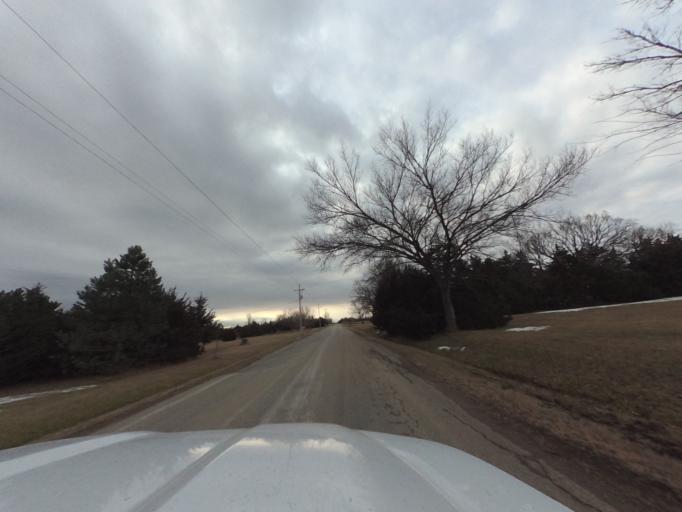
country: US
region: Kansas
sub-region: Chase County
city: Cottonwood Falls
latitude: 38.4289
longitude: -96.3732
